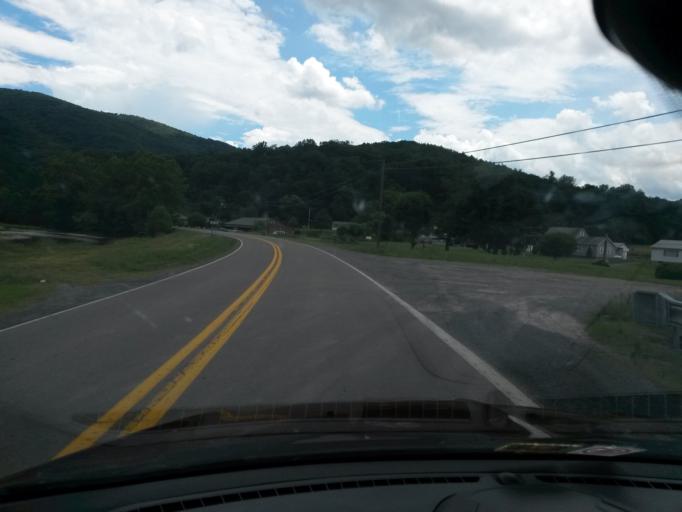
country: US
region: West Virginia
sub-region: Pendleton County
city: Franklin
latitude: 38.7124
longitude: -79.3082
